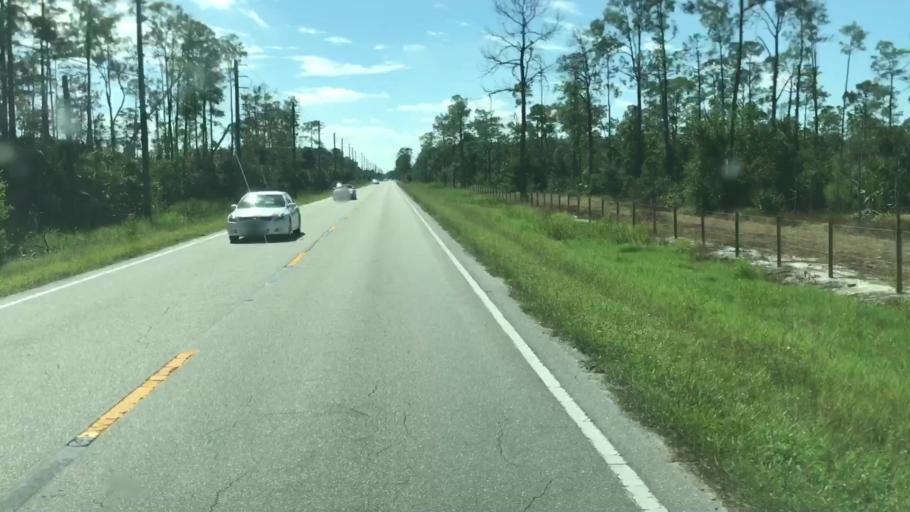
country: US
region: Florida
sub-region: Lee County
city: Bonita Springs
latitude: 26.3422
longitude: -81.7387
